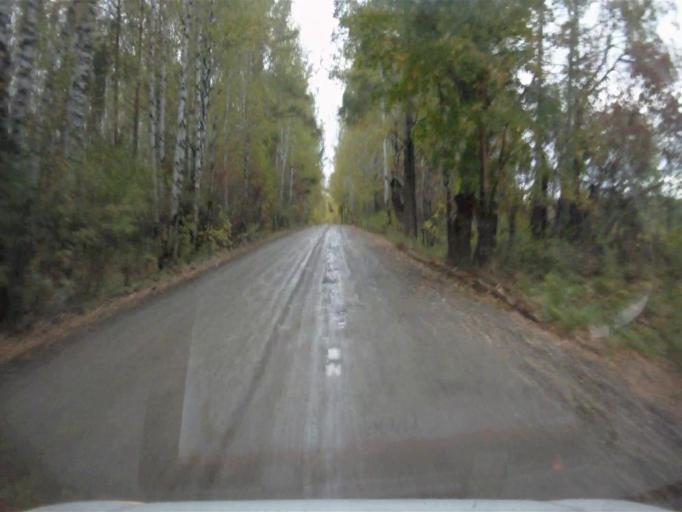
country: RU
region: Sverdlovsk
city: Mikhaylovsk
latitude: 56.1720
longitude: 59.2204
